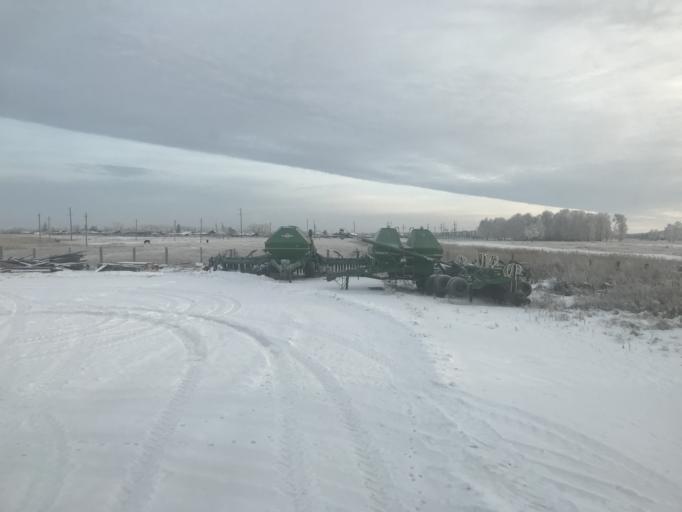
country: KZ
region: Soltustik Qazaqstan
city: Smirnovo
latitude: 54.8474
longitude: 69.7204
